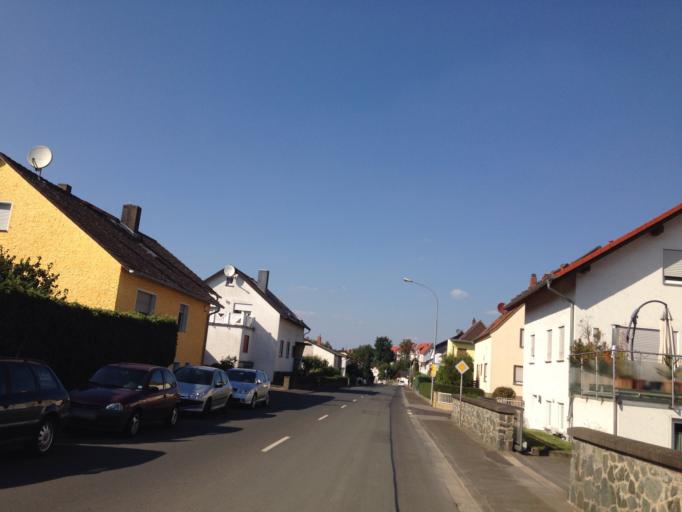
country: DE
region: Hesse
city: Staufenberg
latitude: 50.6448
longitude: 8.7385
